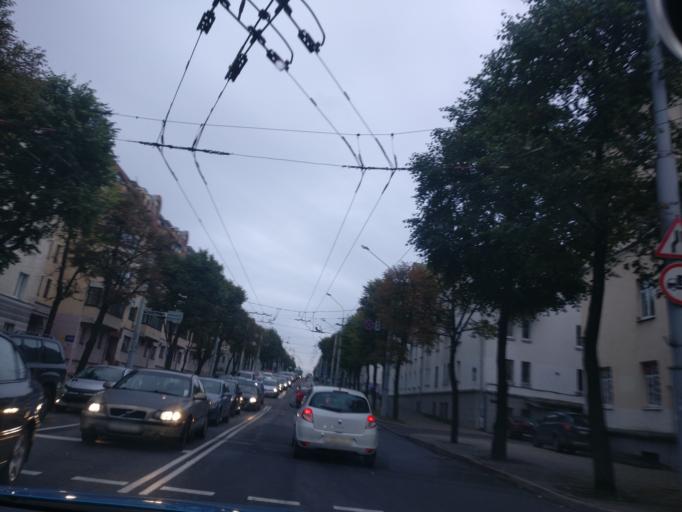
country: BY
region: Minsk
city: Minsk
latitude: 53.9245
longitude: 27.5986
